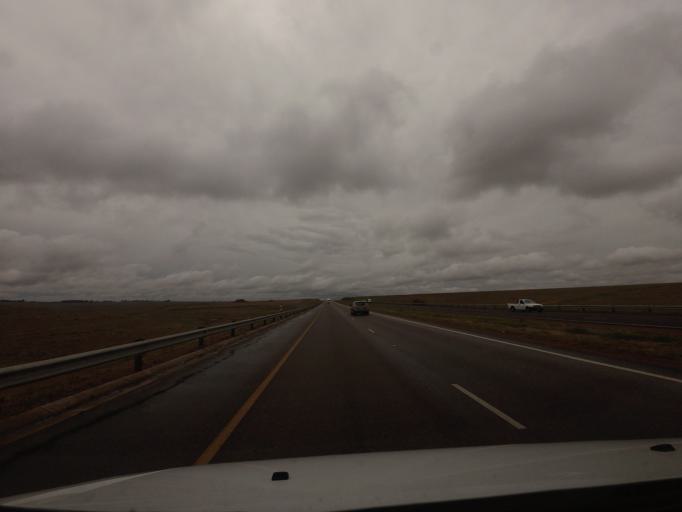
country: ZA
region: Mpumalanga
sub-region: Nkangala District Municipality
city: Middelburg
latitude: -25.8205
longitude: 29.5772
